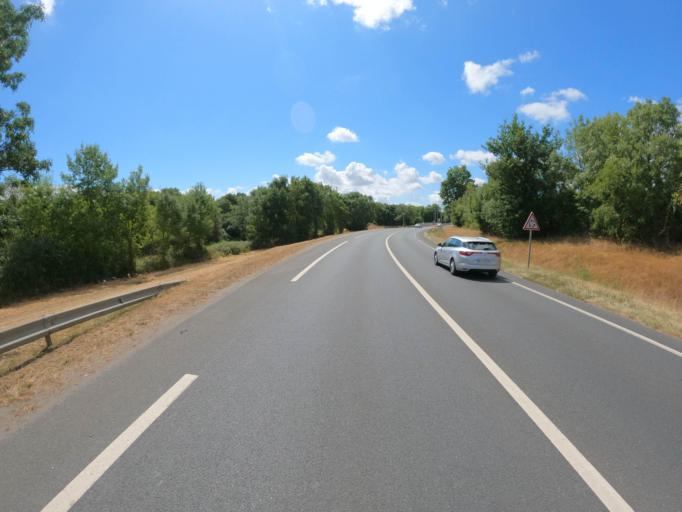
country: FR
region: Pays de la Loire
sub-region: Departement de la Loire-Atlantique
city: Ancenis
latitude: 47.3743
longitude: -1.1669
